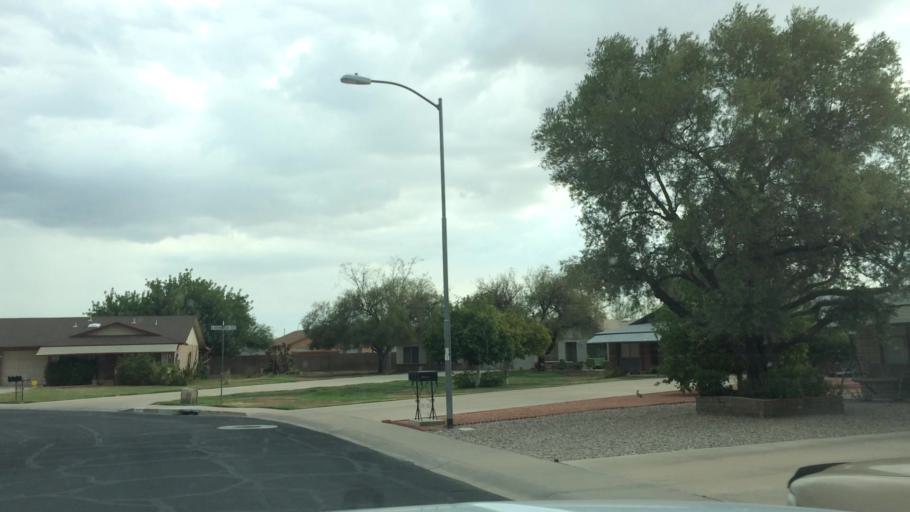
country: US
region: Arizona
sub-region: Maricopa County
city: Sun City
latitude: 33.5741
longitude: -112.2693
